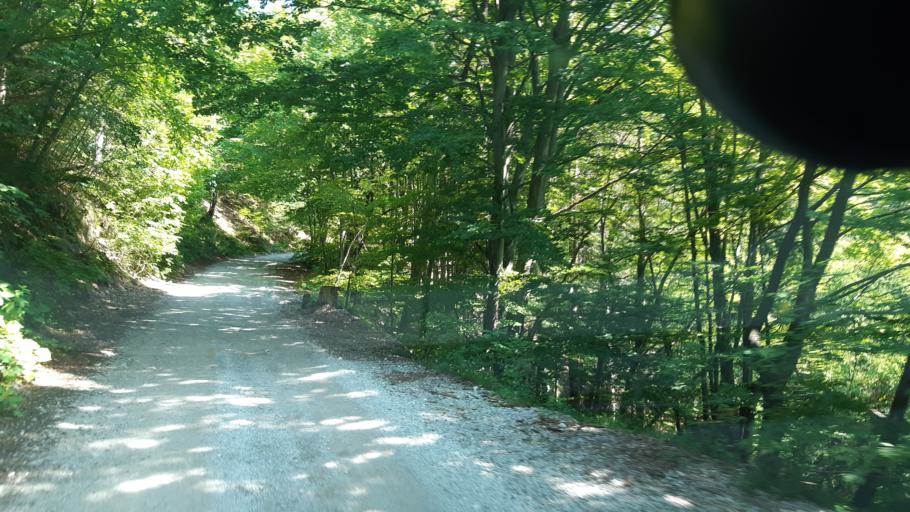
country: SI
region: Trzic
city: Bistrica pri Trzicu
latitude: 46.3666
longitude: 14.2782
